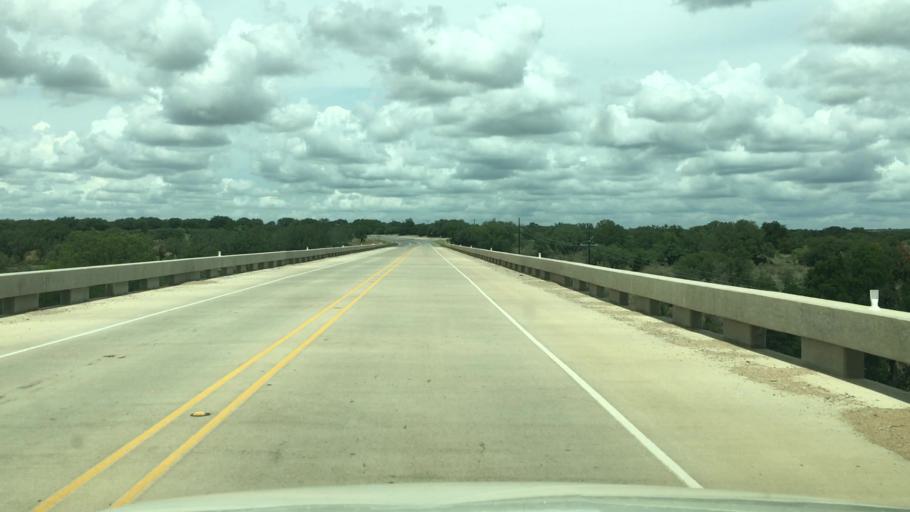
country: US
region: Texas
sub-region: McCulloch County
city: Brady
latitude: 31.0140
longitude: -99.2094
